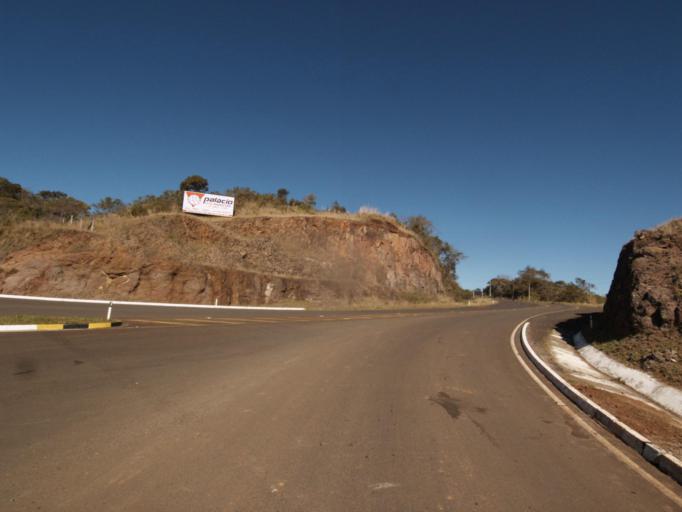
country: AR
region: Misiones
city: Bernardo de Irigoyen
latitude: -26.7050
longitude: -53.5257
